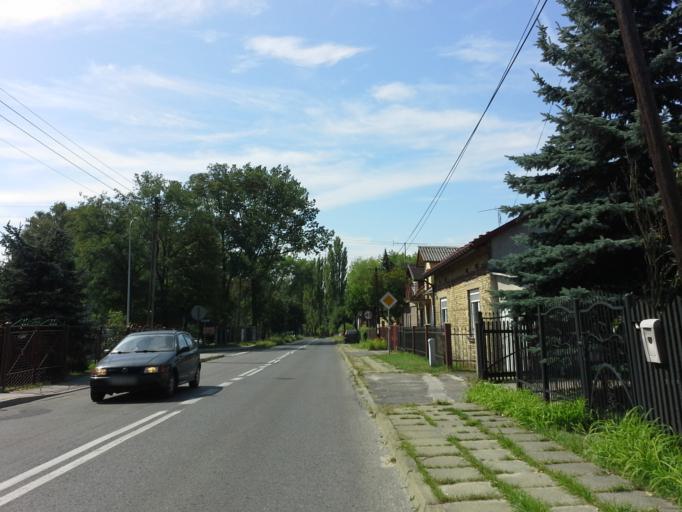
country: PL
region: Lesser Poland Voivodeship
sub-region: Powiat chrzanowski
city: Trzebinia
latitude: 50.1542
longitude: 19.4701
